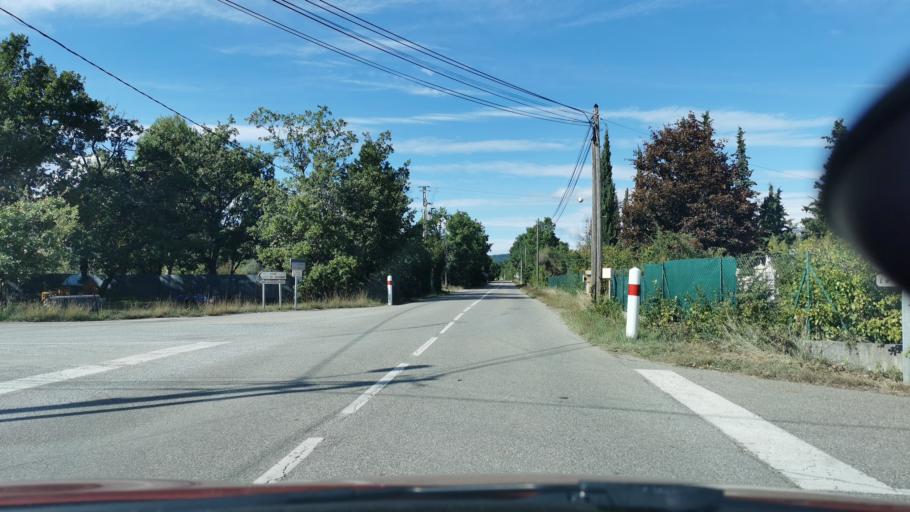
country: FR
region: Provence-Alpes-Cote d'Azur
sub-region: Departement des Alpes-de-Haute-Provence
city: Peipin
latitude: 44.1531
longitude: 5.9751
